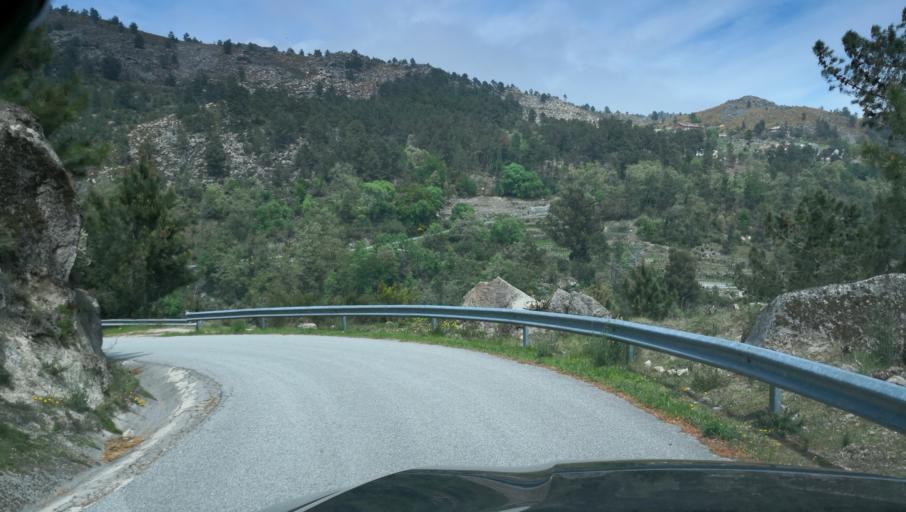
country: PT
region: Vila Real
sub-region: Vila Real
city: Vila Real
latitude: 41.3179
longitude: -7.7950
